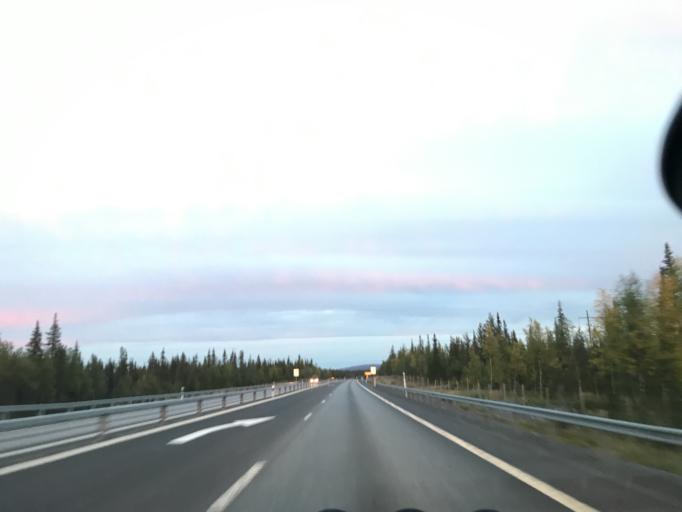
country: SE
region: Norrbotten
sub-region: Gallivare Kommun
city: Malmberget
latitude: 67.6899
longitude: 20.8376
